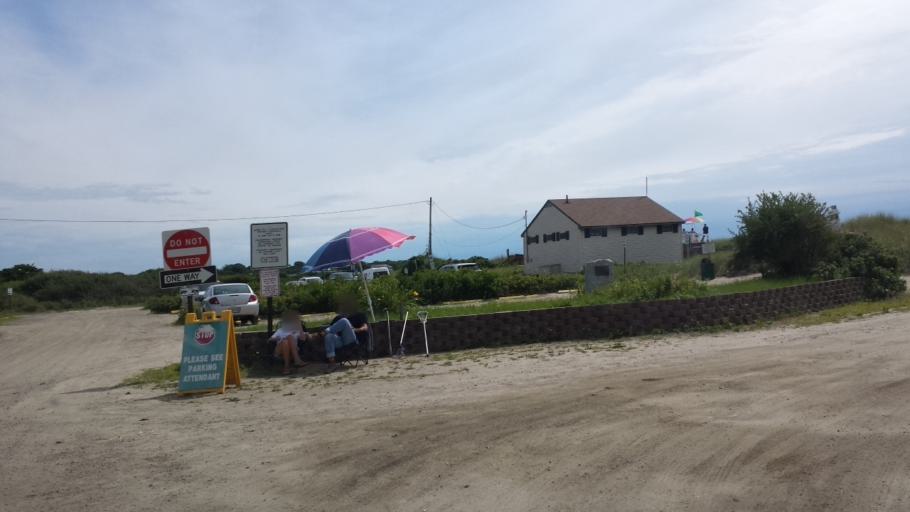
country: US
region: Maine
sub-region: York County
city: Old Orchard Beach
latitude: 43.4423
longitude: -70.3524
